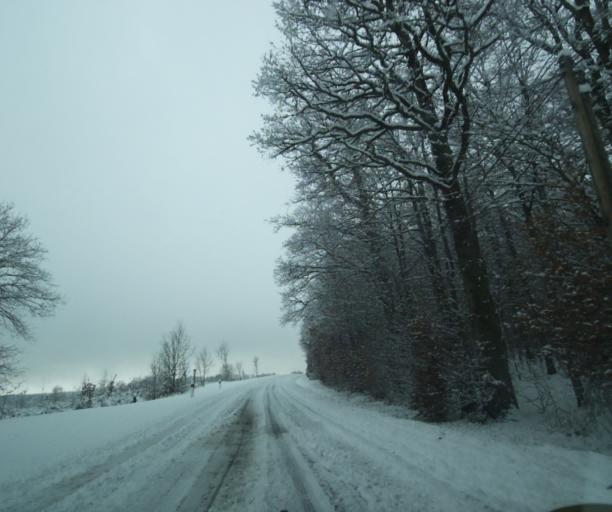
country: FR
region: Champagne-Ardenne
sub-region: Departement de la Haute-Marne
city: Montier-en-Der
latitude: 48.5433
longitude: 4.8020
